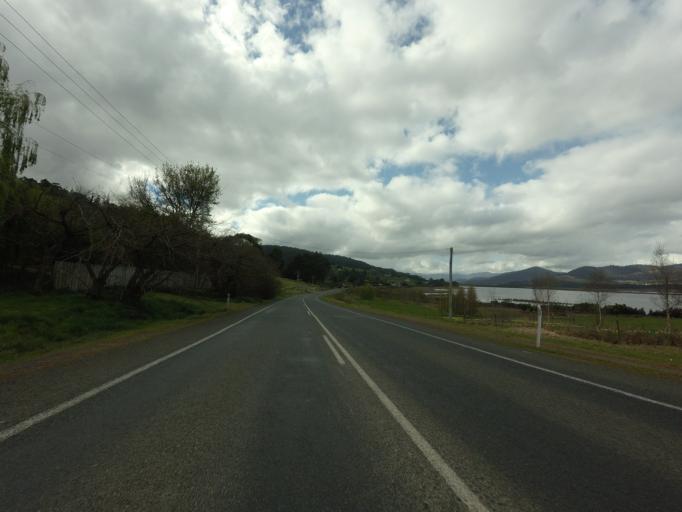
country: AU
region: Tasmania
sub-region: Huon Valley
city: Franklin
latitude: -43.1238
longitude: 146.9896
